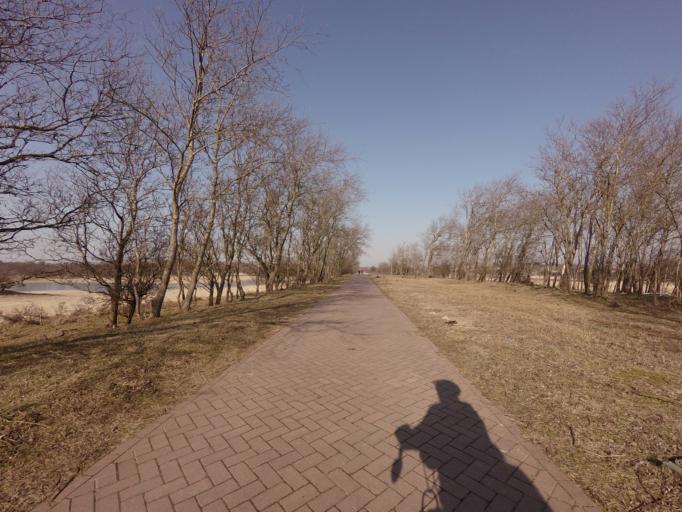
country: NL
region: North Holland
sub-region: Gemeente Bloemendaal
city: Bloemendaal
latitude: 52.4242
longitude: 4.5899
